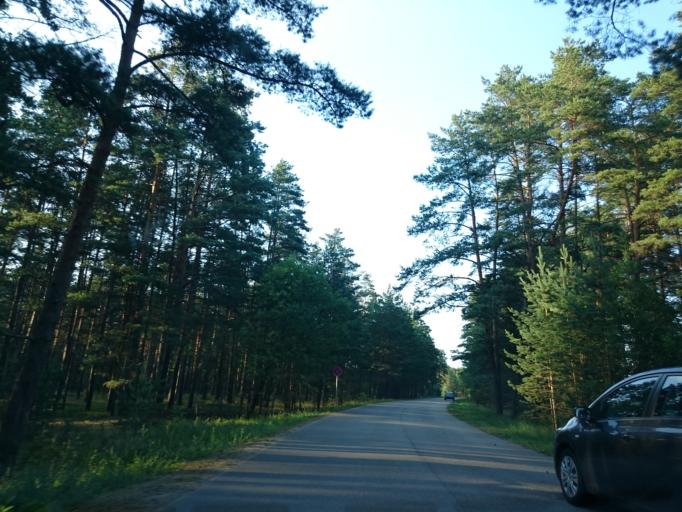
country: LV
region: Carnikava
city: Carnikava
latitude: 57.1770
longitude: 24.3256
